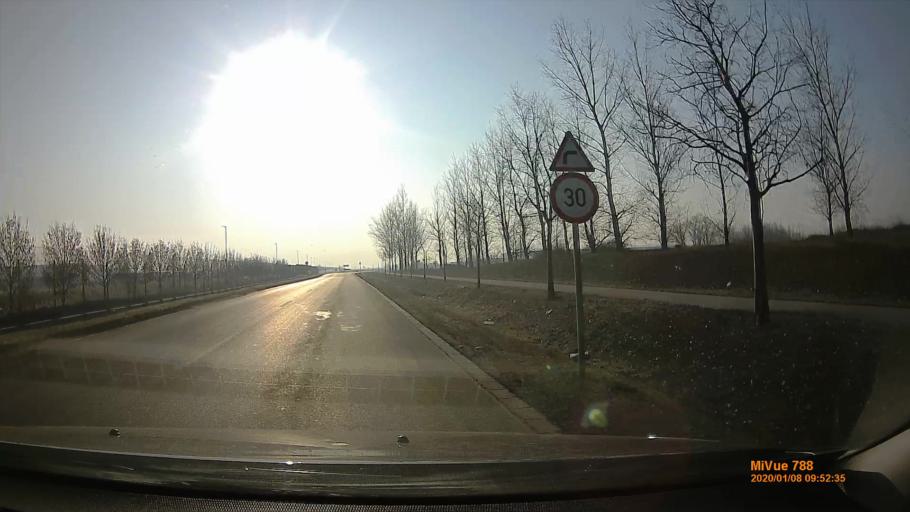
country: HU
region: Bacs-Kiskun
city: Kecskemet
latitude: 46.8668
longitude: 19.7048
